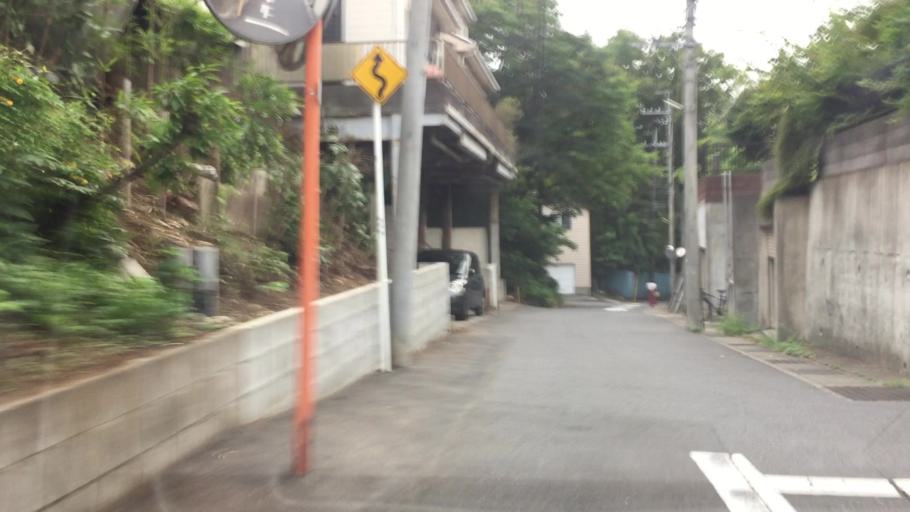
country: JP
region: Chiba
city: Matsudo
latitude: 35.7989
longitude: 139.9299
